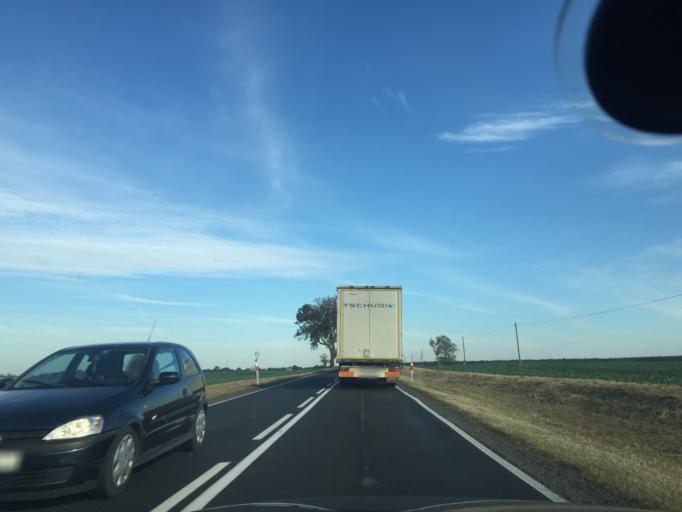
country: PL
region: Kujawsko-Pomorskie
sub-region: Powiat mogilenski
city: Strzelno
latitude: 52.6221
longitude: 18.0644
